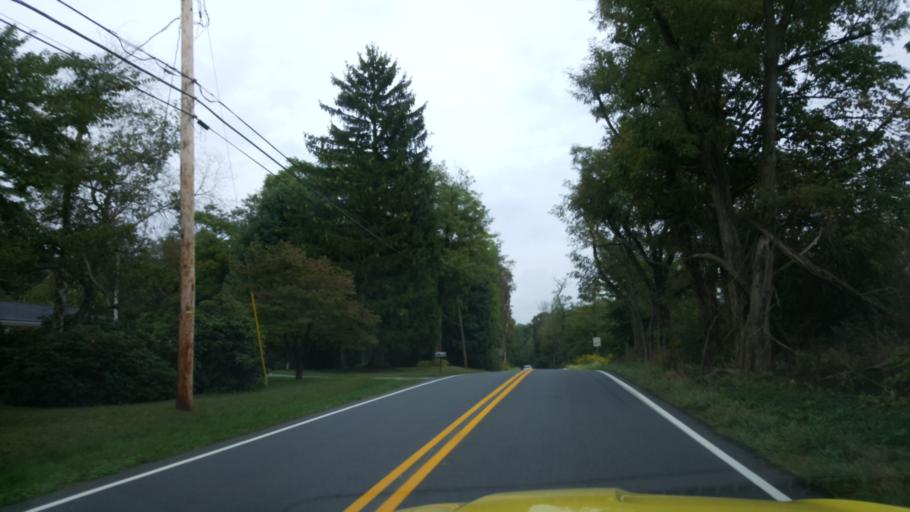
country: US
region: Pennsylvania
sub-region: Lebanon County
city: Campbelltown
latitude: 40.2454
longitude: -76.5249
